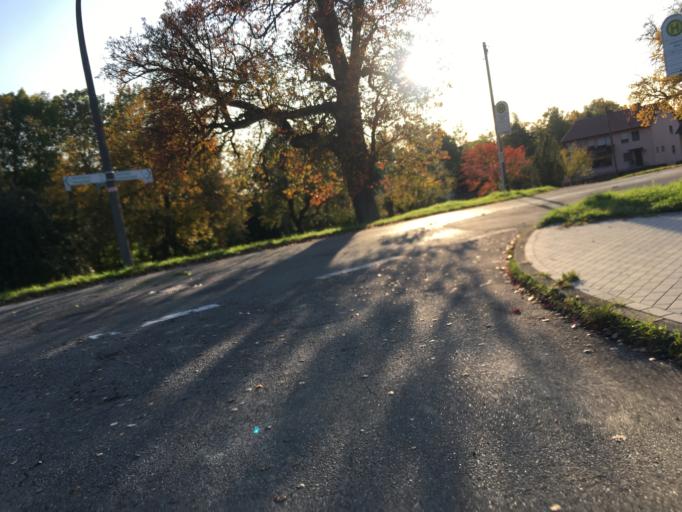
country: DE
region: Baden-Wuerttemberg
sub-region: Regierungsbezirk Stuttgart
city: Neuenstein
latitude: 49.2357
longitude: 9.6147
